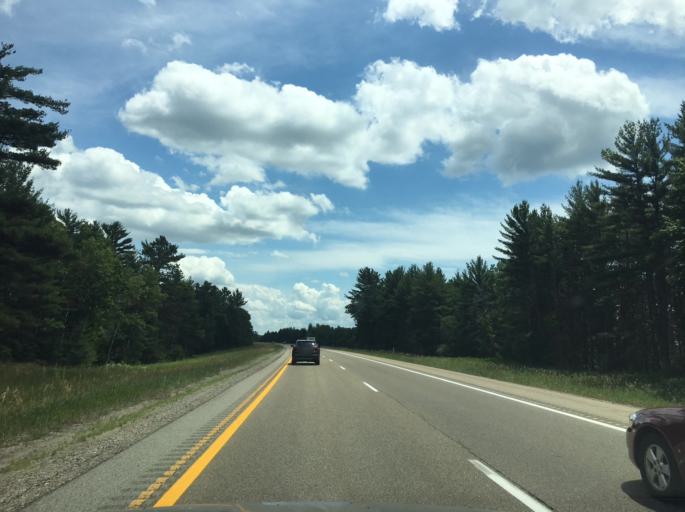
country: US
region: Michigan
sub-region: Crawford County
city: Grayling
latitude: 44.5460
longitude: -84.7000
